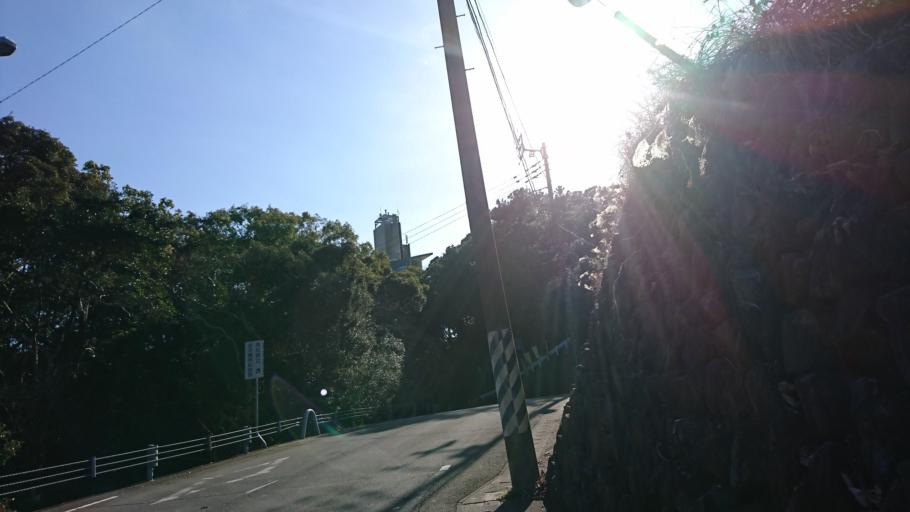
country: JP
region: Kochi
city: Kochi-shi
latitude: 33.4979
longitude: 133.5726
